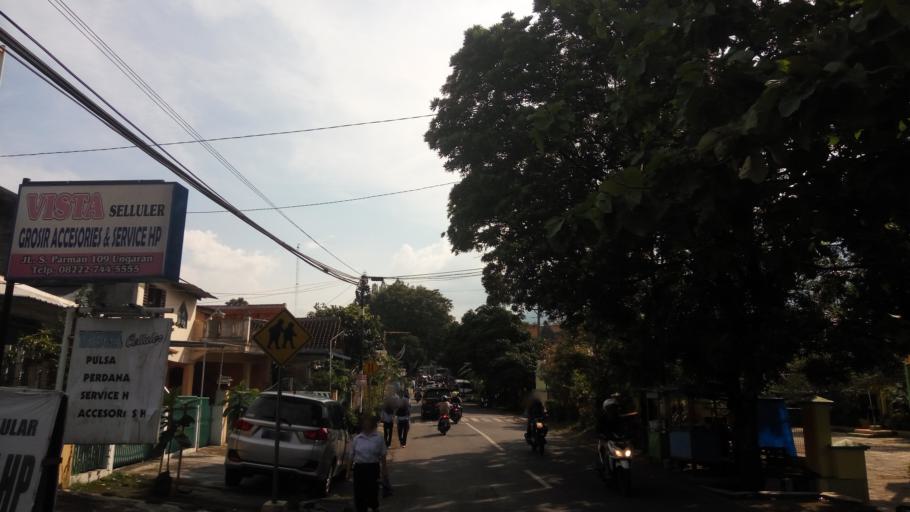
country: ID
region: Central Java
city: Ungaran
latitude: -7.1450
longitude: 110.4098
